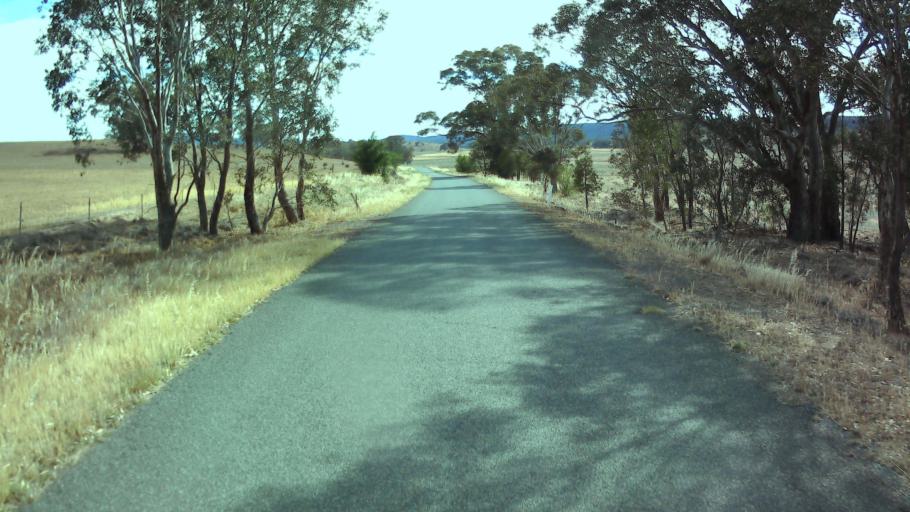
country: AU
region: New South Wales
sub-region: Weddin
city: Grenfell
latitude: -33.8264
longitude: 148.2858
